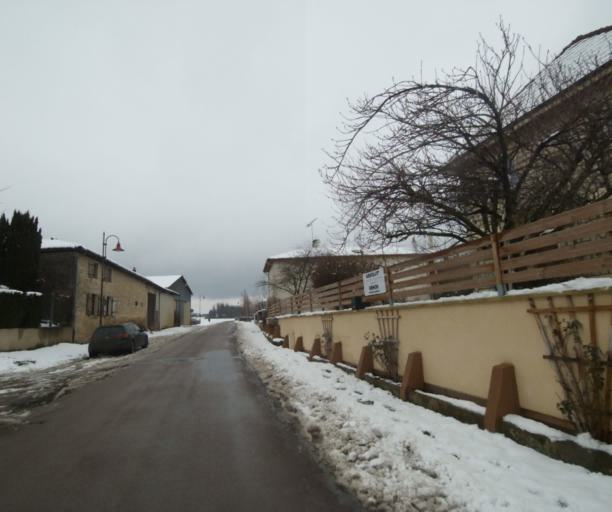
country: FR
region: Champagne-Ardenne
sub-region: Departement de la Haute-Marne
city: Laneuville-a-Remy
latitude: 48.5060
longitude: 4.8683
